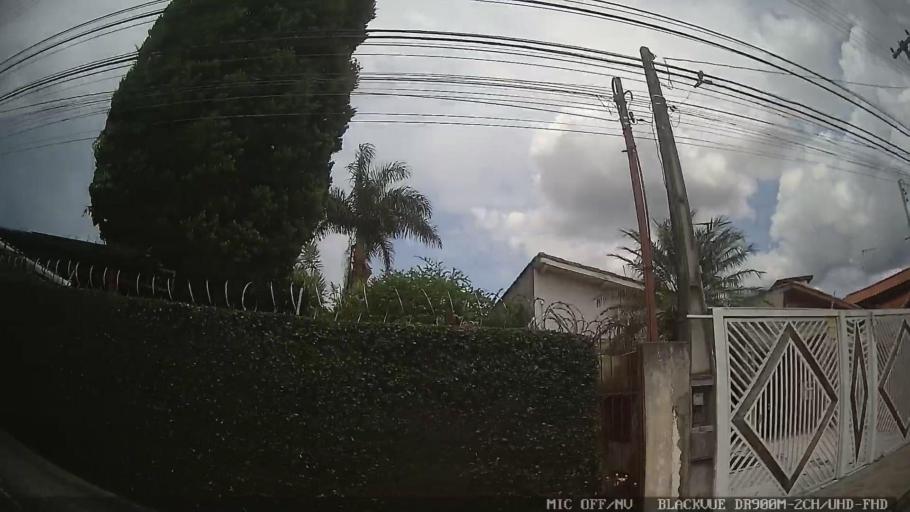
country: BR
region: Sao Paulo
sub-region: Suzano
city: Suzano
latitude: -23.5365
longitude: -46.3158
